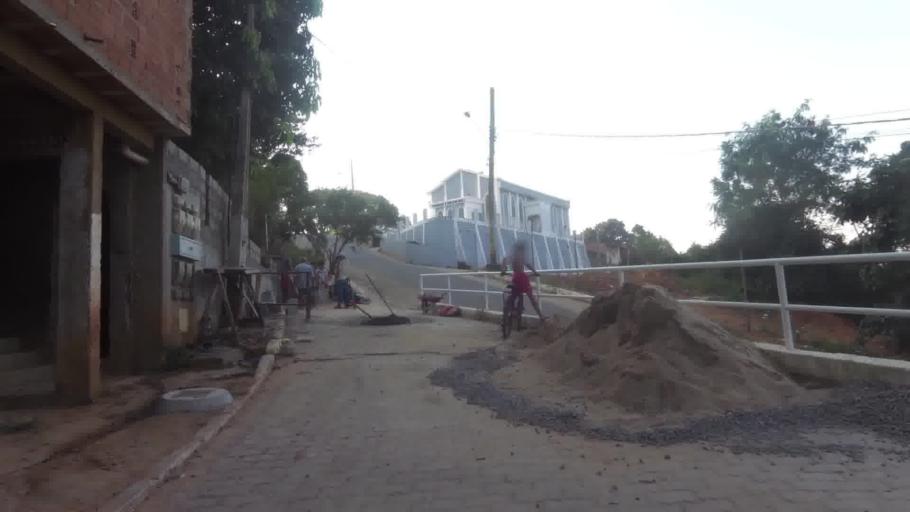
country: BR
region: Espirito Santo
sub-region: Piuma
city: Piuma
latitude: -20.8341
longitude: -40.7187
